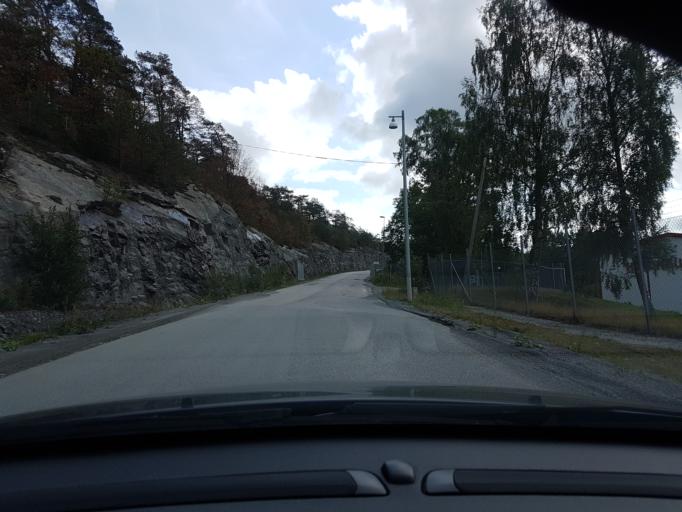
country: SE
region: Vaestra Goetaland
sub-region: Ale Kommun
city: Nodinge-Nol
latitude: 57.8709
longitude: 12.0348
